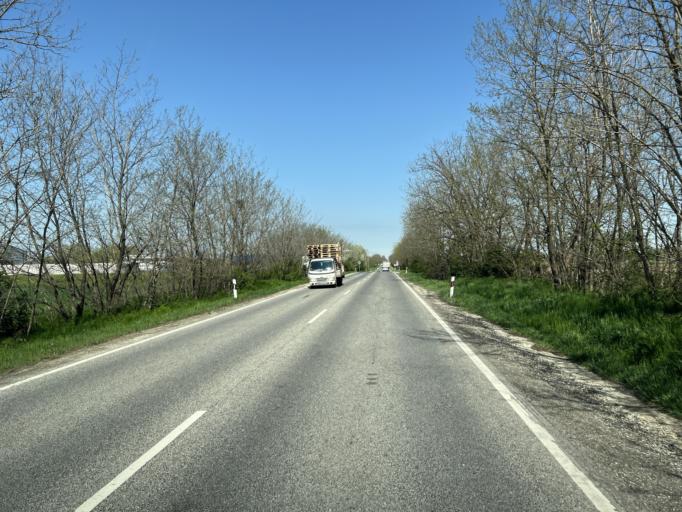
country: HU
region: Pest
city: Alsonemedi
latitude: 47.3310
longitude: 19.1843
